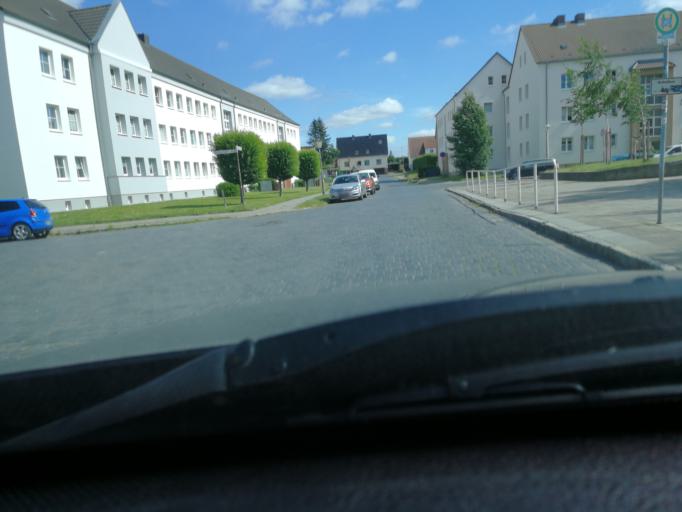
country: DE
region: Mecklenburg-Vorpommern
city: Stralsund
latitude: 54.3038
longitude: 13.0671
